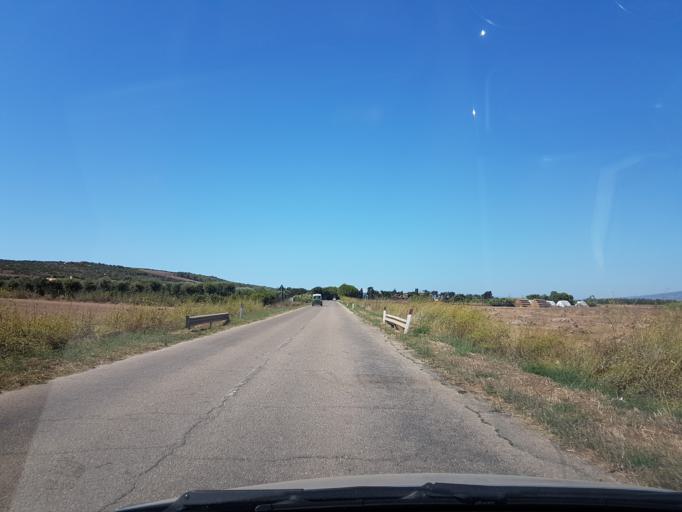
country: IT
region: Sardinia
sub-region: Provincia di Oristano
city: Cabras
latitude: 39.9401
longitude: 8.4580
